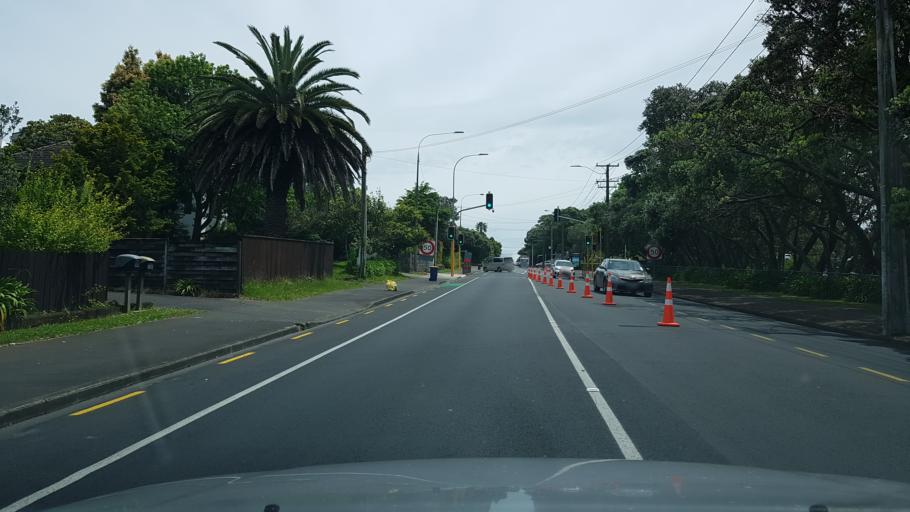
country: NZ
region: Auckland
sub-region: Auckland
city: North Shore
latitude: -36.8021
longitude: 174.7872
